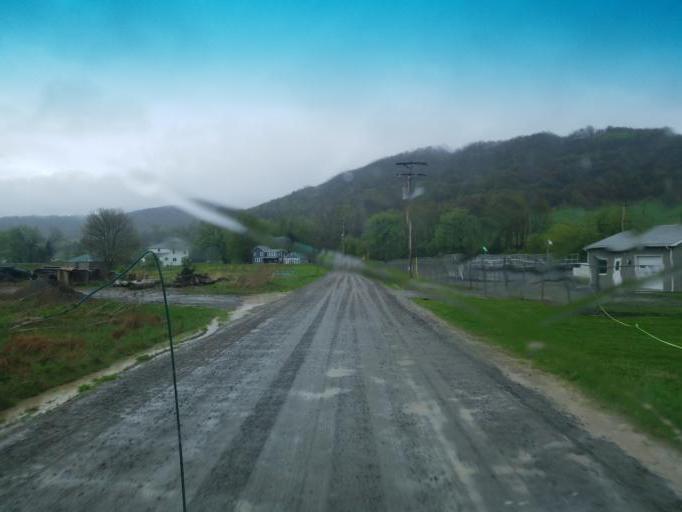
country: US
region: Pennsylvania
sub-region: Tioga County
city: Westfield
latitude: 41.9183
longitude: -77.6243
